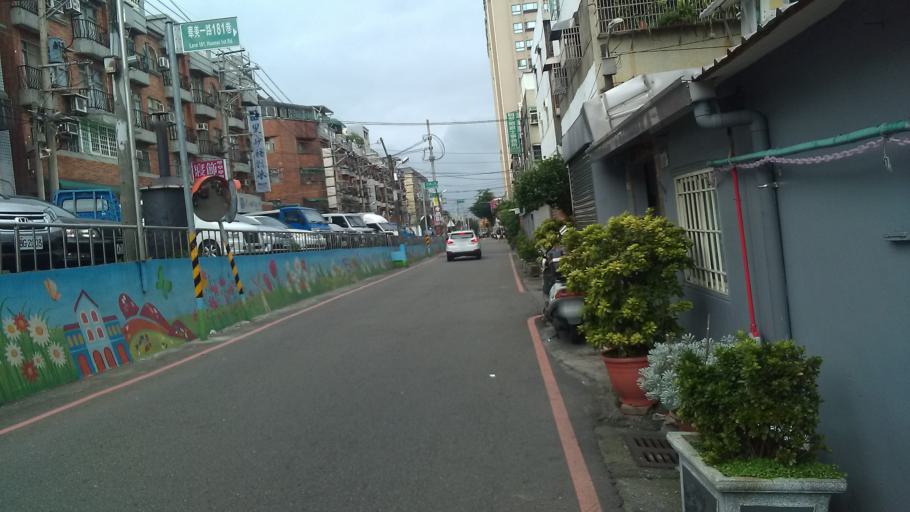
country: TW
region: Taiwan
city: Taoyuan City
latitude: 24.9519
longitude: 121.2607
